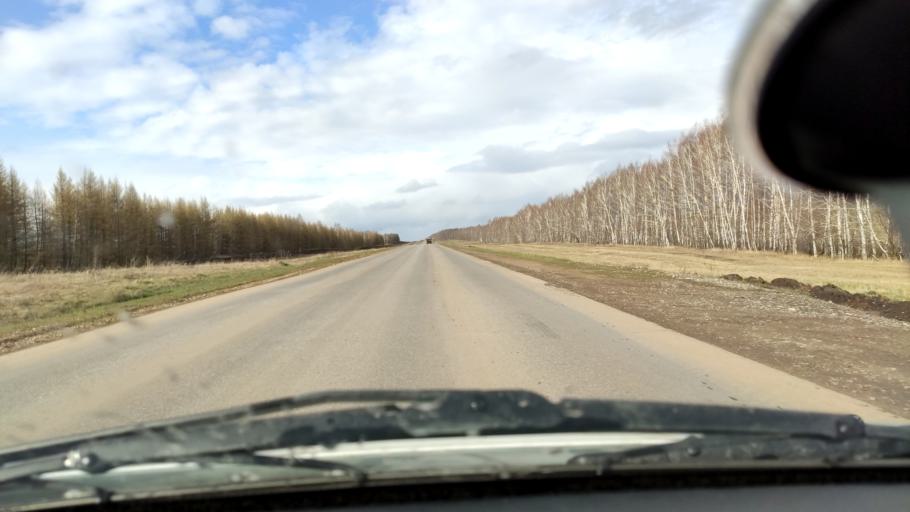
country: RU
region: Bashkortostan
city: Buzdyak
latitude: 54.6946
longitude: 54.5593
